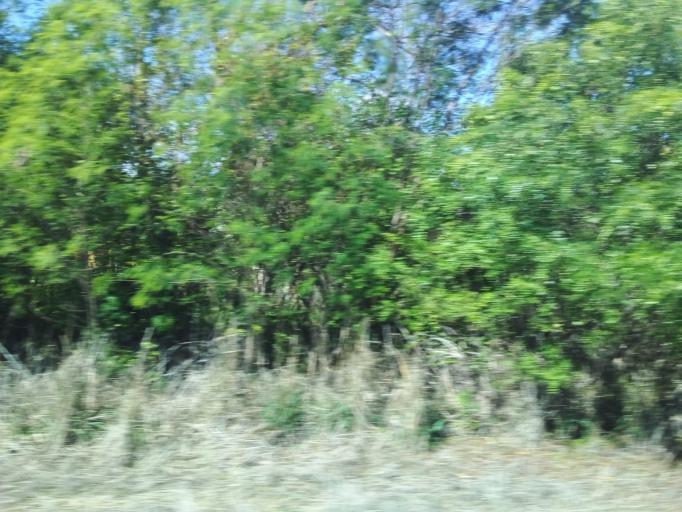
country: BR
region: Minas Gerais
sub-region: Governador Valadares
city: Governador Valadares
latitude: -18.8421
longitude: -41.8740
